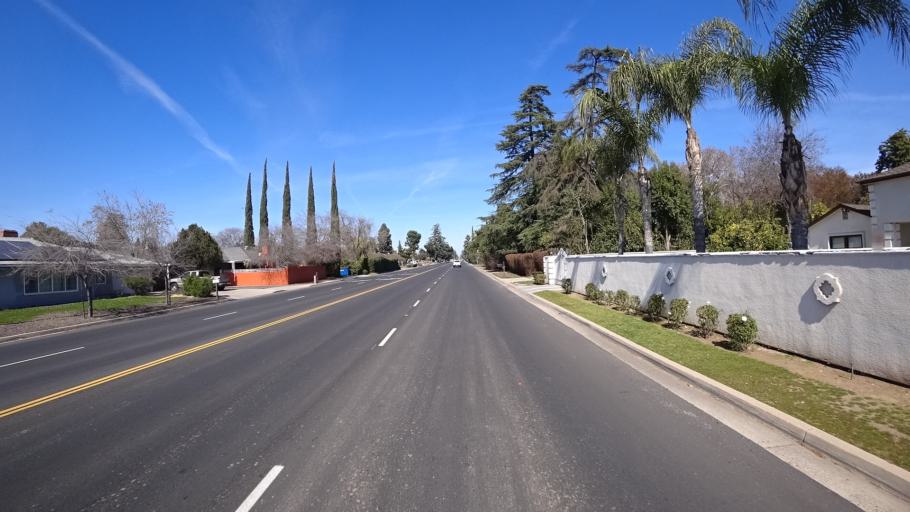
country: US
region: California
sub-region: Fresno County
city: Fresno
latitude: 36.8020
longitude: -119.8085
